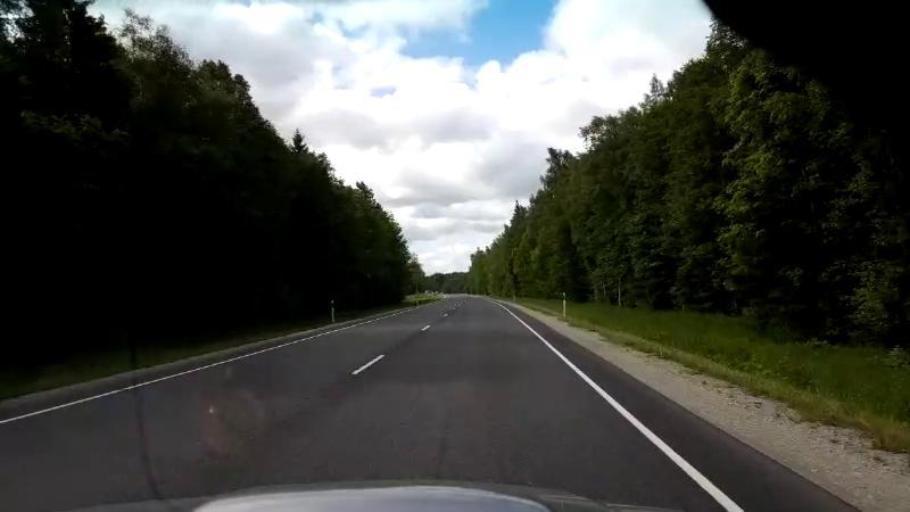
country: EE
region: Raplamaa
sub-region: Maerjamaa vald
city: Marjamaa
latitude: 58.8235
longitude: 24.4141
